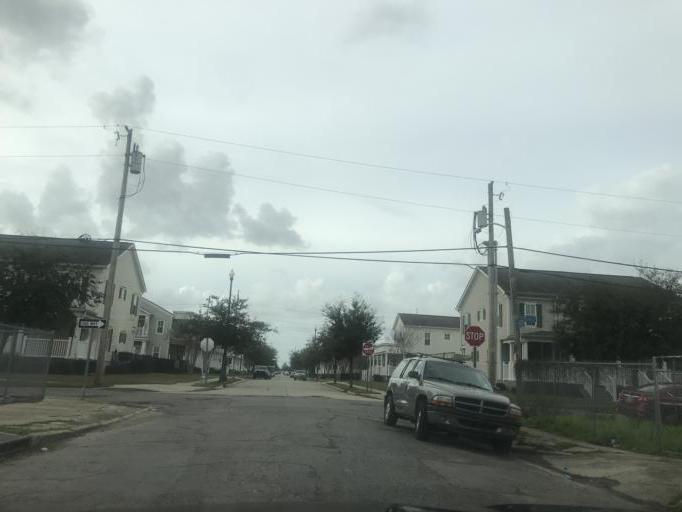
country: US
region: Louisiana
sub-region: Orleans Parish
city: New Orleans
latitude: 29.9486
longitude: -90.0906
